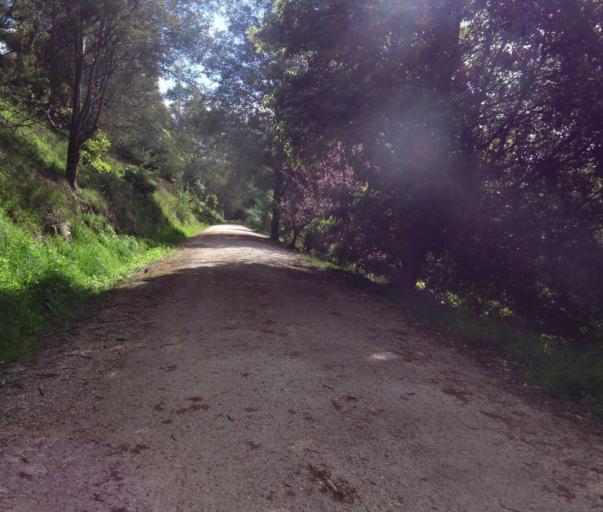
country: AU
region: Victoria
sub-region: Bass Coast
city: North Wonthaggi
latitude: -38.5642
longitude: 145.9639
